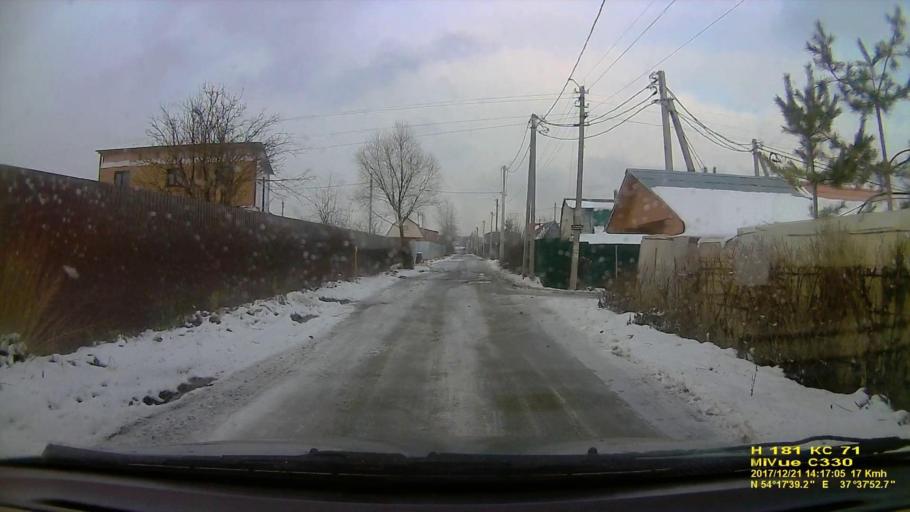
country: RU
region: Tula
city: Gorelki
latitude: 54.2943
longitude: 37.6314
